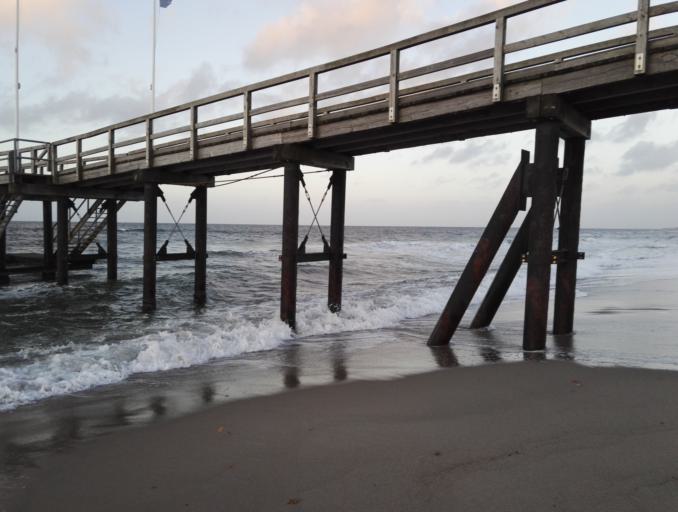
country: DE
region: Schleswig-Holstein
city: Wangels
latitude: 54.3129
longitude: 10.7914
